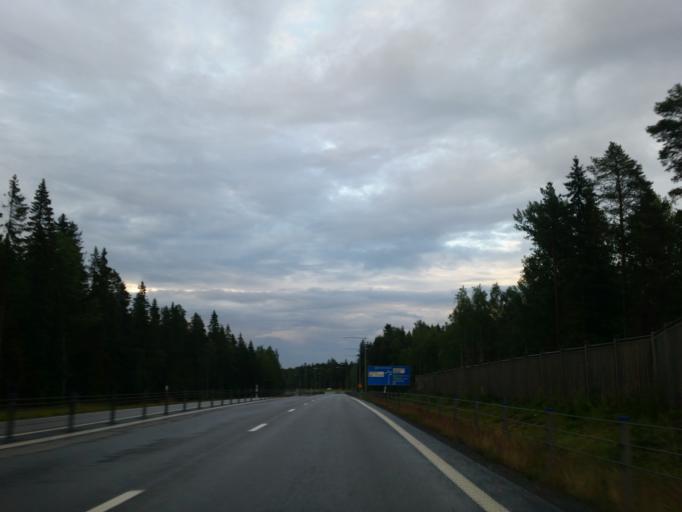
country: SE
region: Vaesterbotten
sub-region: Umea Kommun
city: Ersmark
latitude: 63.8475
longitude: 20.3328
